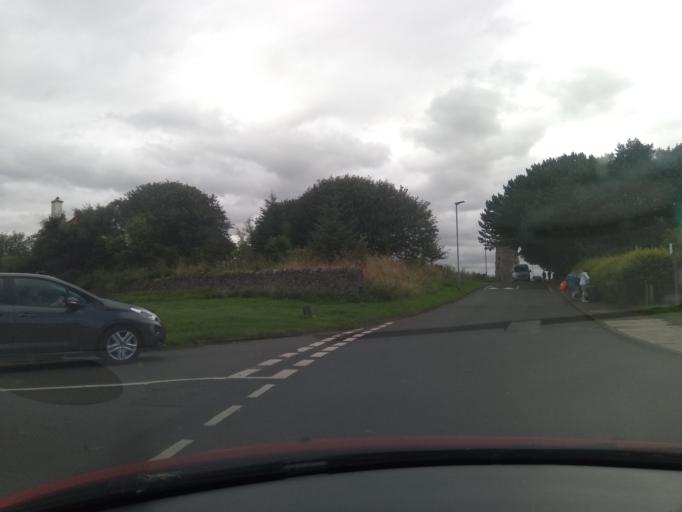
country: GB
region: England
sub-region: Northumberland
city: Berwick-Upon-Tweed
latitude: 55.7765
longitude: -2.0034
